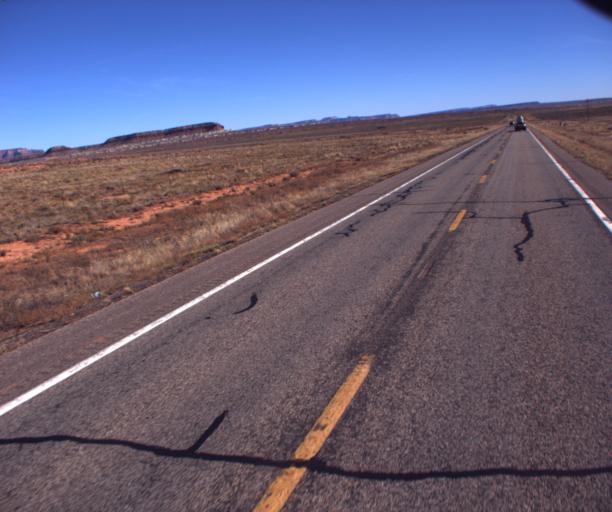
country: US
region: Arizona
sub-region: Coconino County
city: Fredonia
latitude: 36.8902
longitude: -112.6218
